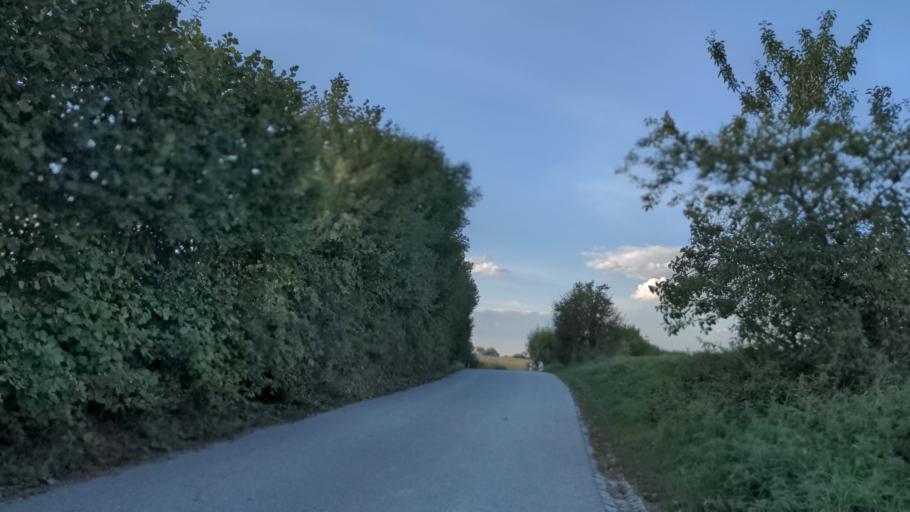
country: DE
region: Schleswig-Holstein
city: Ahrensbok
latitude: 53.9808
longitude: 10.6268
